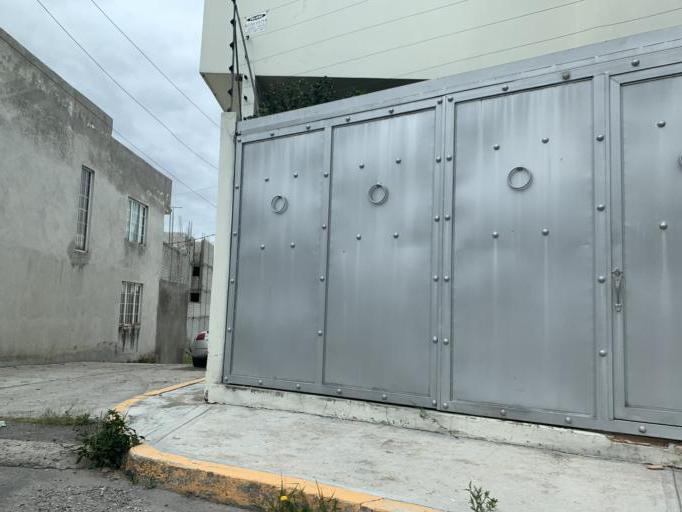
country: MX
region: Puebla
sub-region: Puebla
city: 18 de Marzo
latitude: 18.9807
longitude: -98.1935
